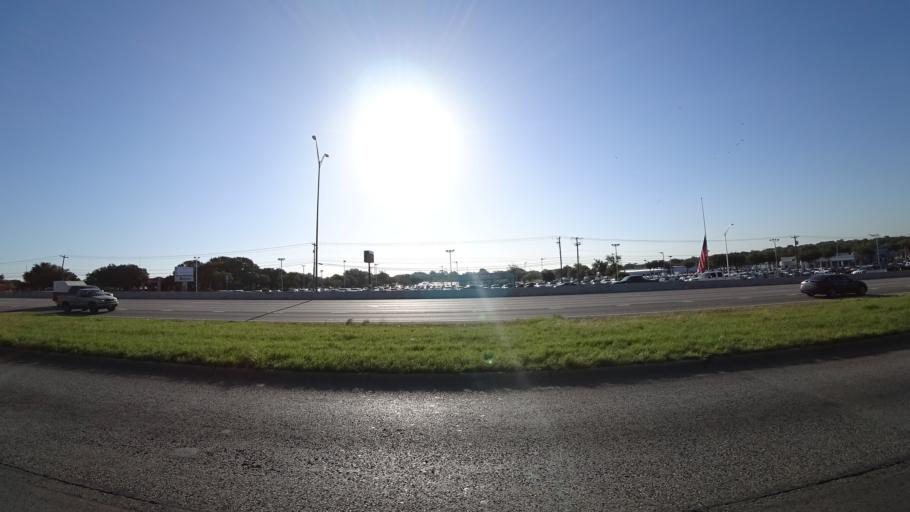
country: US
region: Texas
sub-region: Travis County
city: Wells Branch
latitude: 30.3534
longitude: -97.6915
